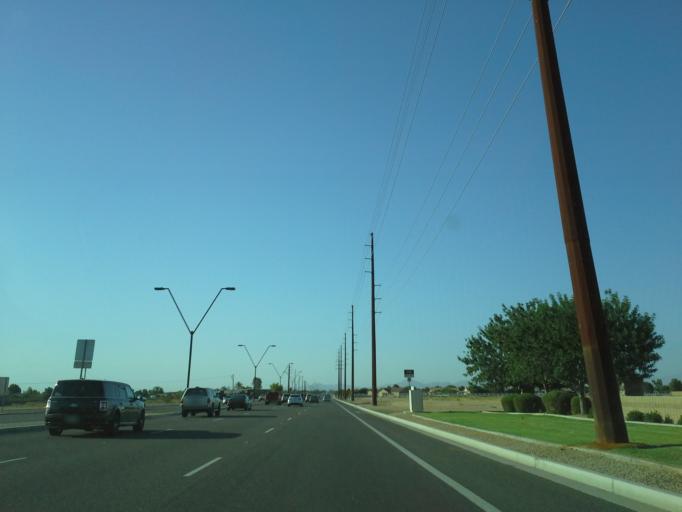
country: US
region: Arizona
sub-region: Maricopa County
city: Queen Creek
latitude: 33.2088
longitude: -111.6343
